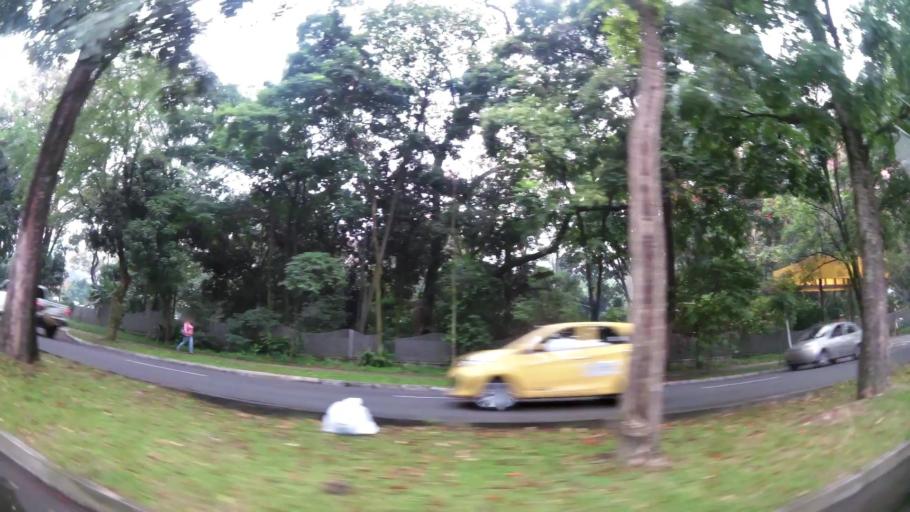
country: CO
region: Antioquia
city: Medellin
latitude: 6.2195
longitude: -75.5718
